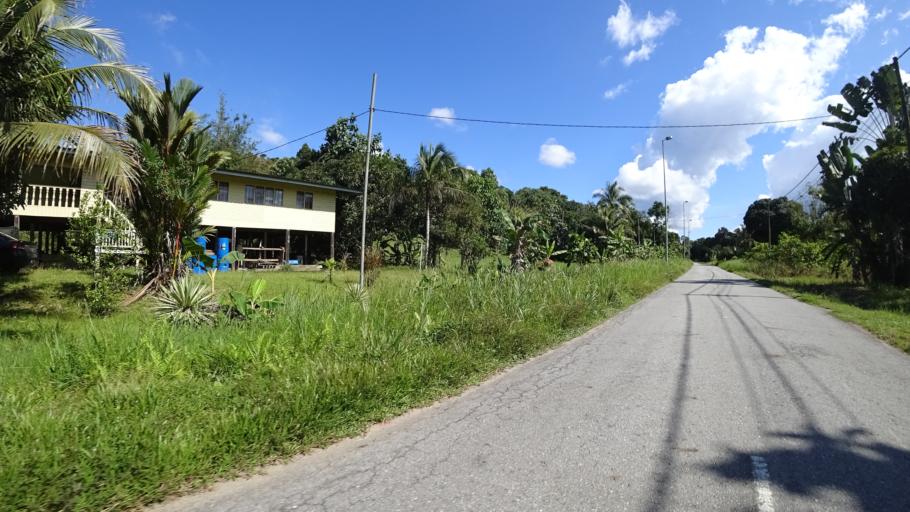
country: BN
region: Tutong
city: Tutong
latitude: 4.7483
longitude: 114.7841
